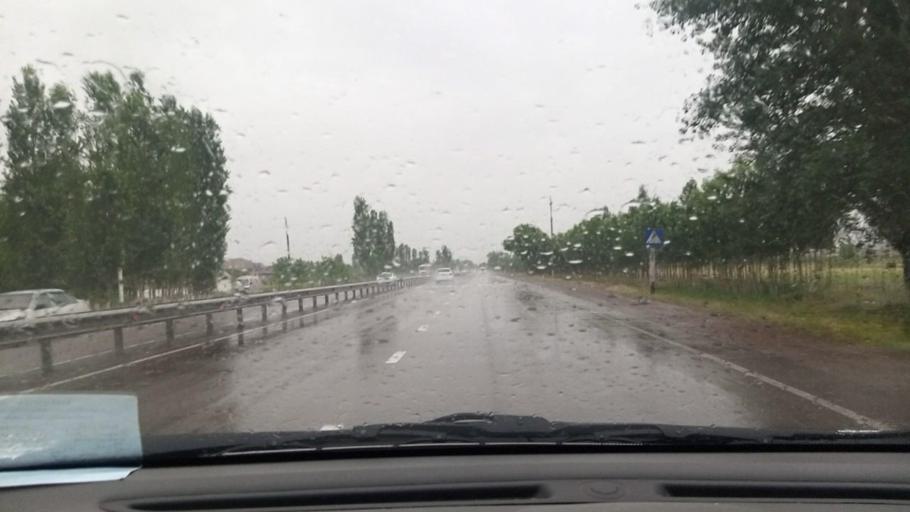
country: UZ
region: Toshkent
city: Ohangaron
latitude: 40.9086
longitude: 69.7794
